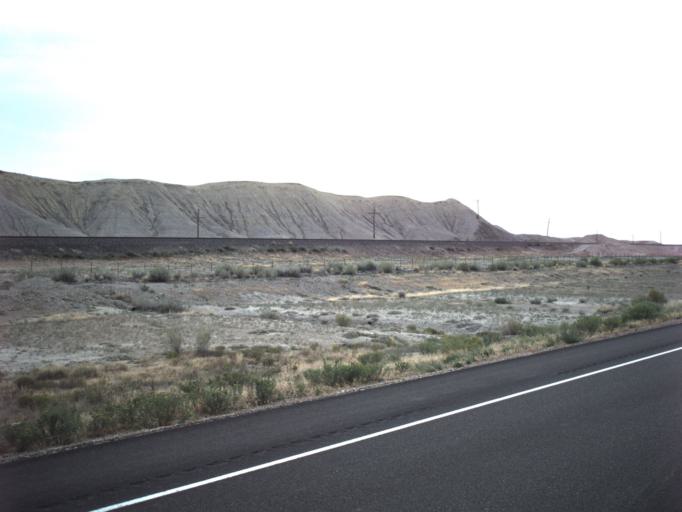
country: US
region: Utah
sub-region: Carbon County
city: East Carbon City
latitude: 39.0394
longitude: -110.3073
